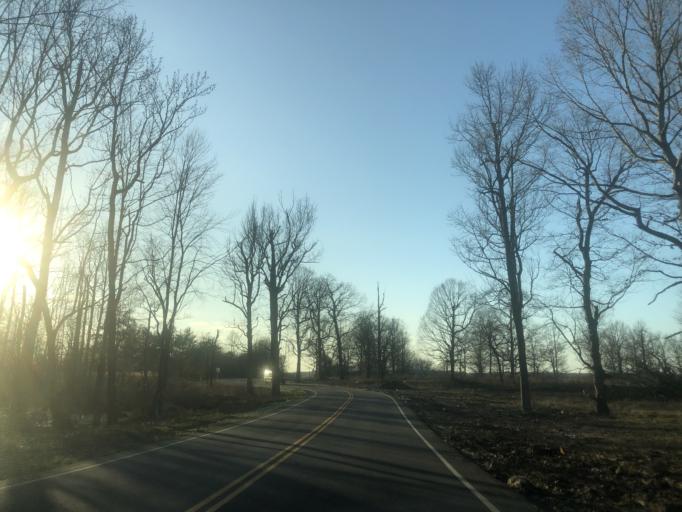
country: US
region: Tennessee
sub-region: Sumner County
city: White House
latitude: 36.4813
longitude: -86.6968
